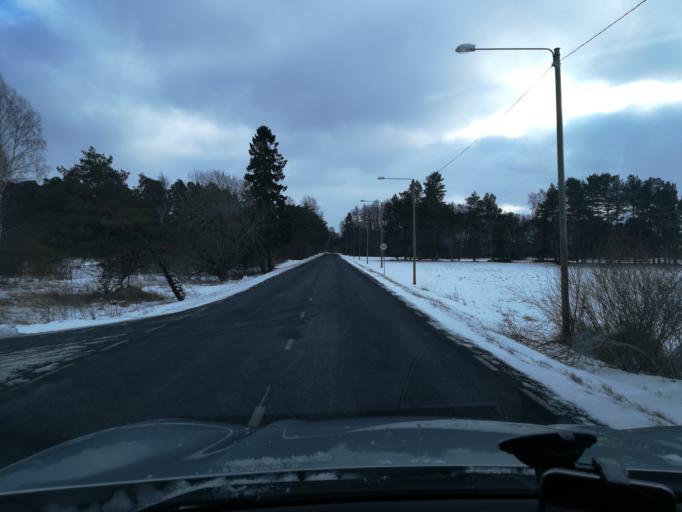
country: EE
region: Harju
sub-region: Keila linn
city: Keila
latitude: 59.3954
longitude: 24.4127
